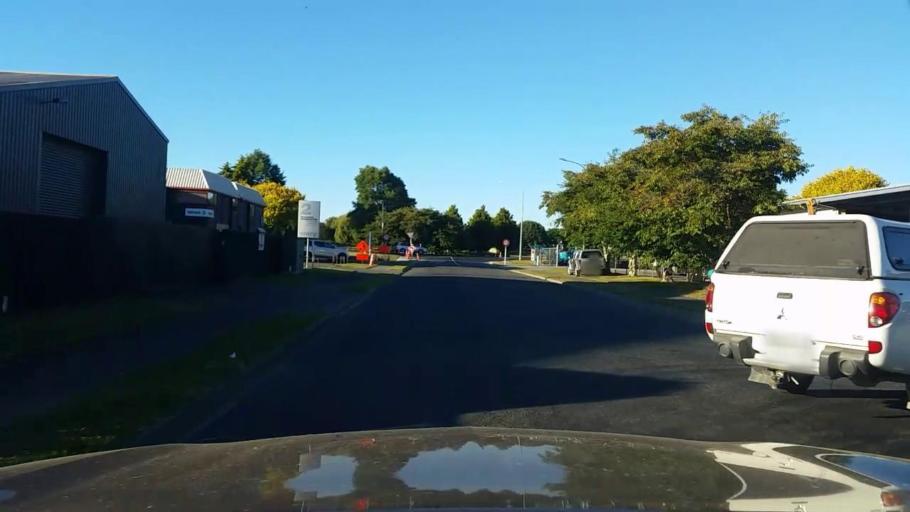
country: NZ
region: Waikato
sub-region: Matamata-Piako District
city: Matamata
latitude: -37.8151
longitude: 175.7893
